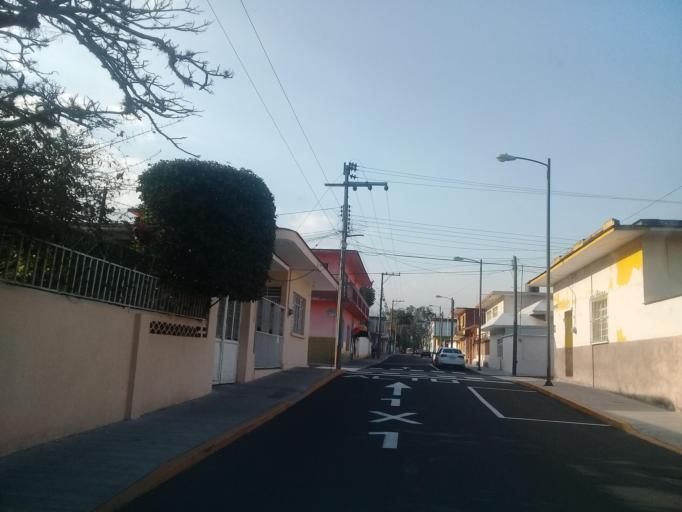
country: MX
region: Veracruz
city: Orizaba
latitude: 18.8516
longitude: -97.1123
